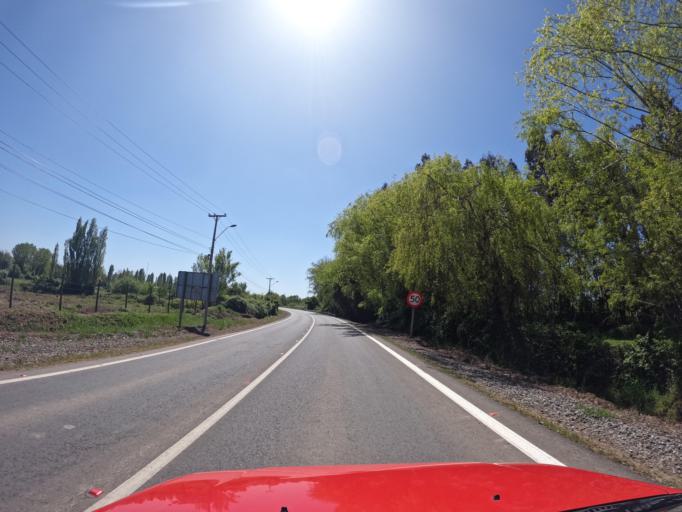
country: CL
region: Maule
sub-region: Provincia de Linares
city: Colbun
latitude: -35.7527
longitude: -71.4175
